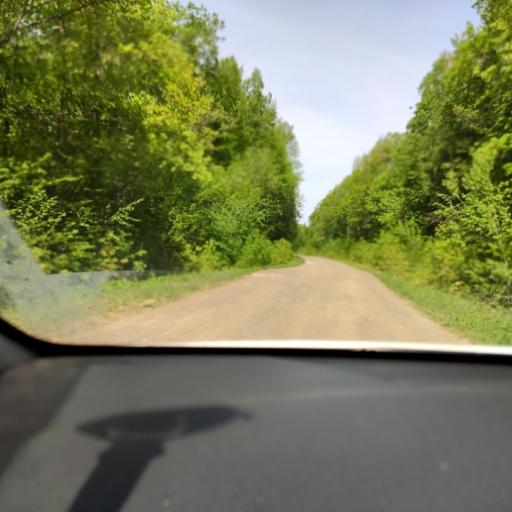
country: RU
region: Tatarstan
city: Sviyazhsk
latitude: 55.7480
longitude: 48.8062
